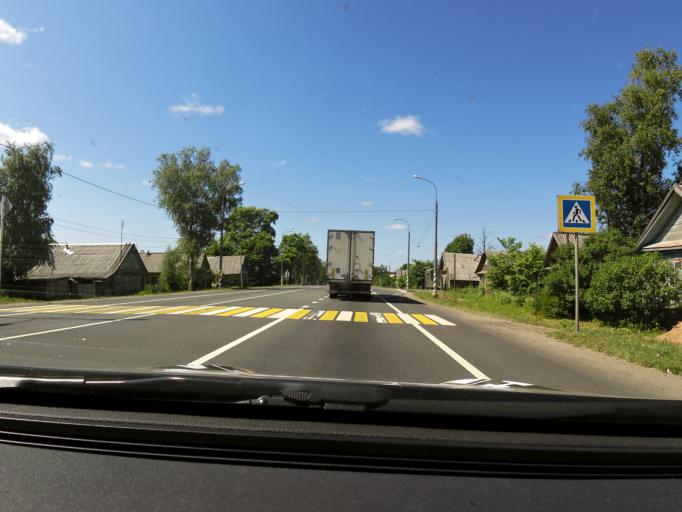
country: RU
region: Novgorod
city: Kresttsy
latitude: 58.1432
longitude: 32.7652
